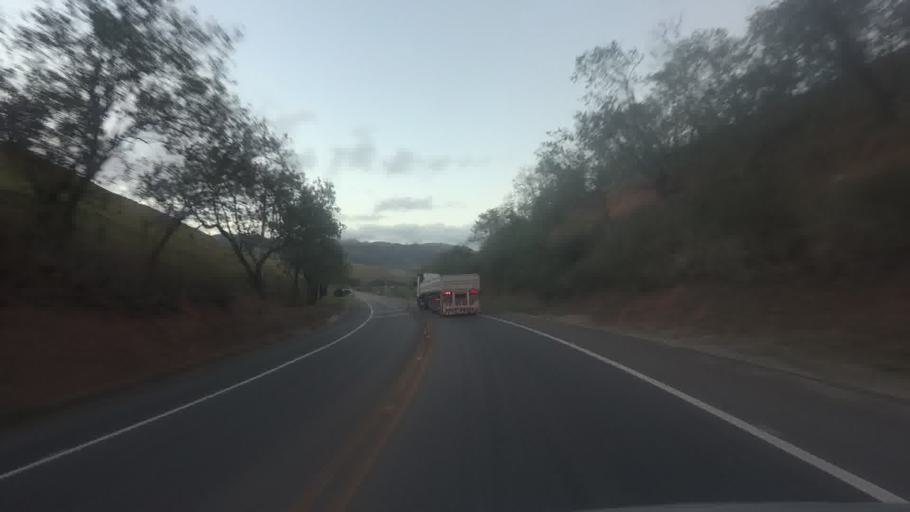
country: BR
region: Espirito Santo
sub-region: Rio Novo Do Sul
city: Rio Novo do Sul
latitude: -20.8604
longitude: -40.8760
